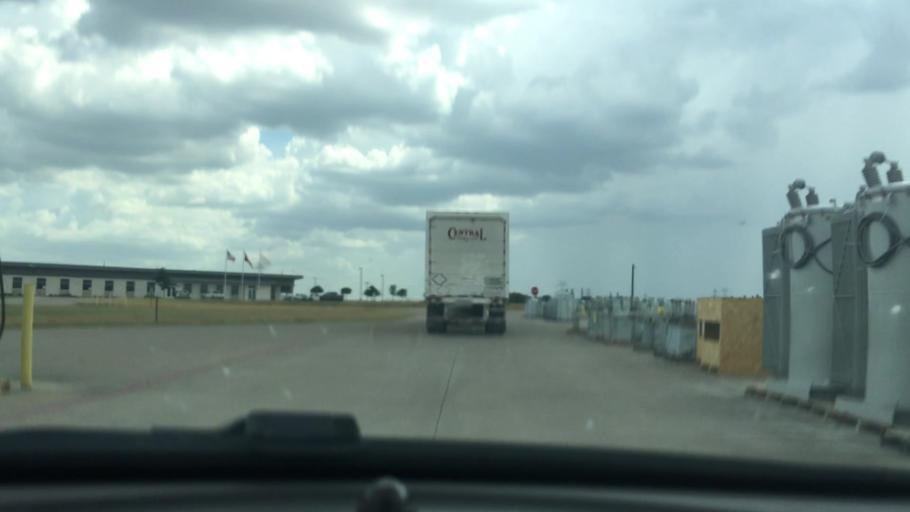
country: US
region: Texas
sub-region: Dallas County
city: Lancaster
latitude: 32.5639
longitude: -96.7695
